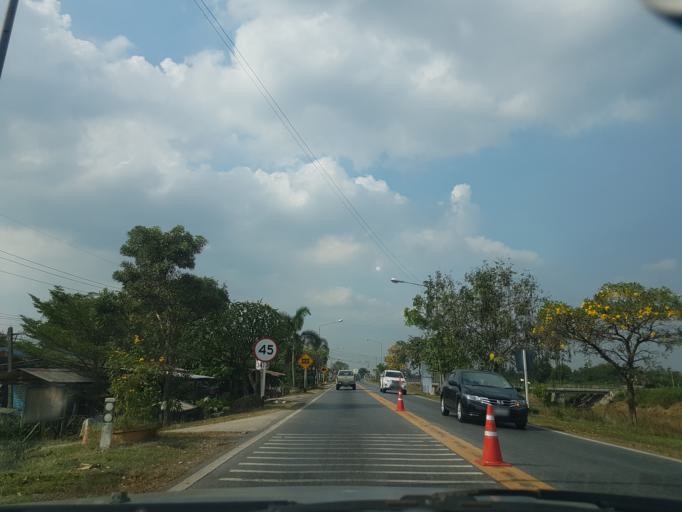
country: TH
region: Phra Nakhon Si Ayutthaya
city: Phachi
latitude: 14.4675
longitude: 100.7501
